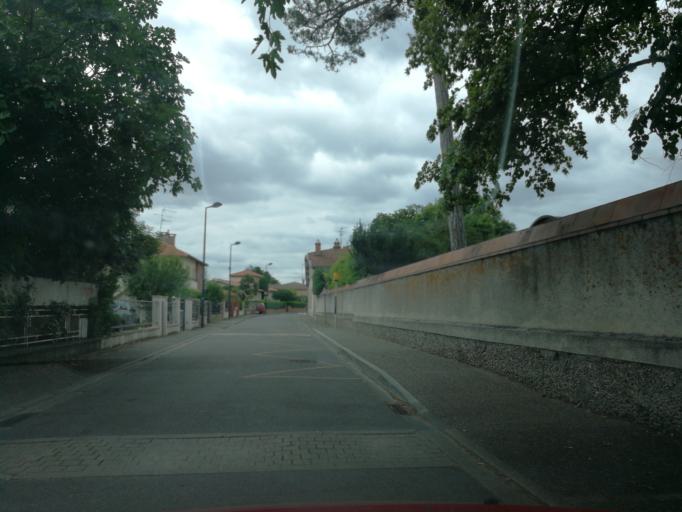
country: FR
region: Midi-Pyrenees
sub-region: Departement de la Haute-Garonne
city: Auzeville-Tolosane
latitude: 43.5298
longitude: 1.4797
